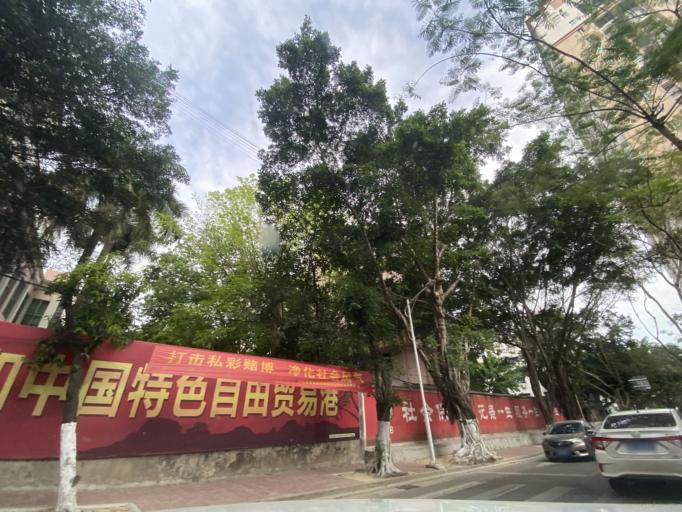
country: CN
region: Hainan
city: Baocheng
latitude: 18.6418
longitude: 109.6958
